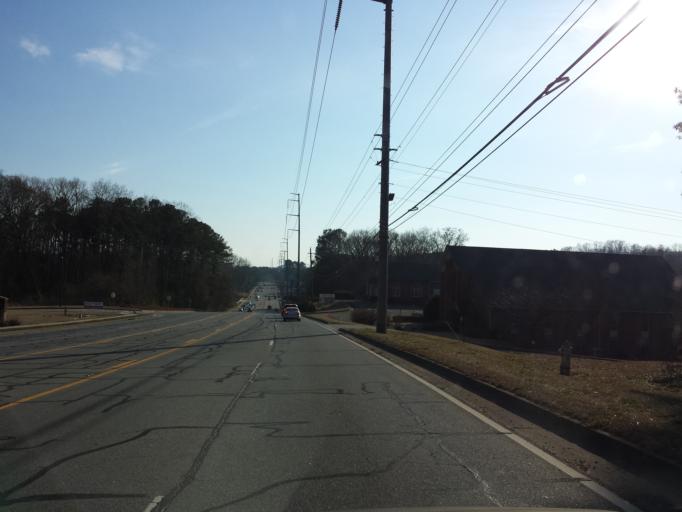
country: US
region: Georgia
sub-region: Cherokee County
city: Woodstock
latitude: 34.0532
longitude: -84.5248
